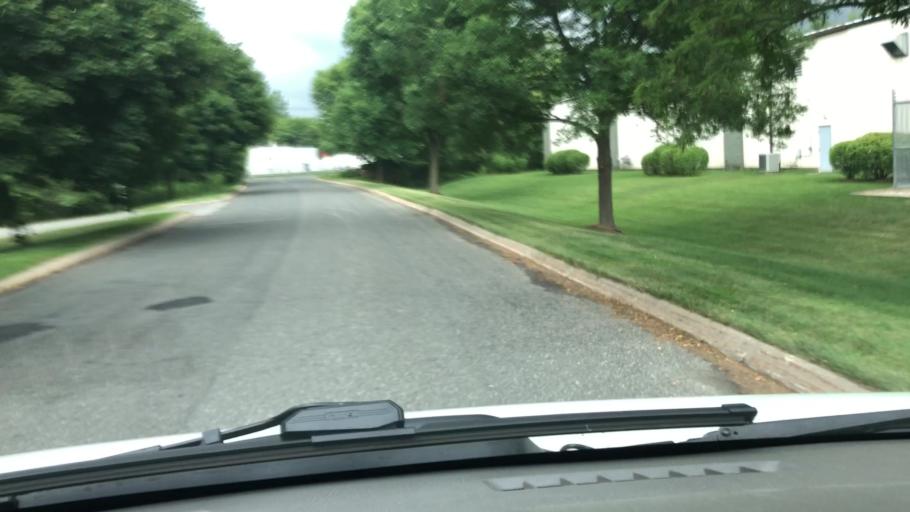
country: US
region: Massachusetts
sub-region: Berkshire County
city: Adams
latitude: 42.6384
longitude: -73.1101
